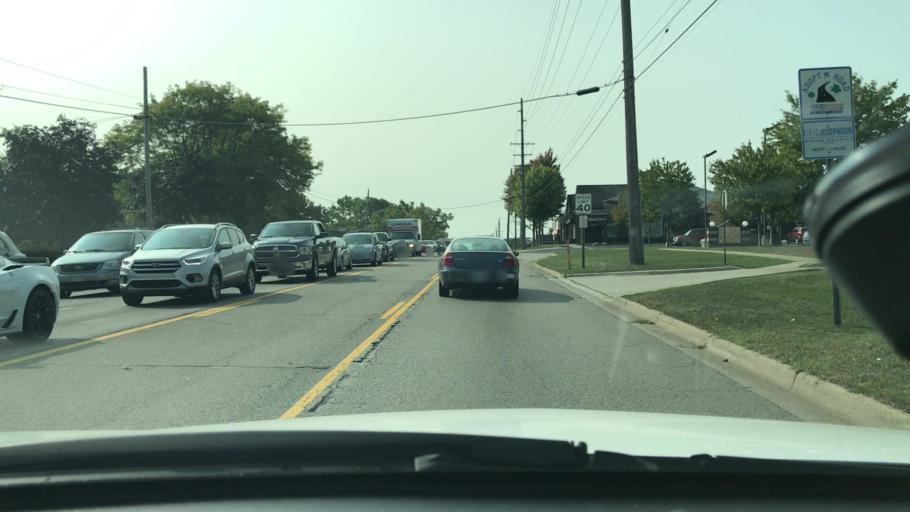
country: US
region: Michigan
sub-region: Oakland County
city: Wolverine Lake
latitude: 42.5987
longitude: -83.4463
